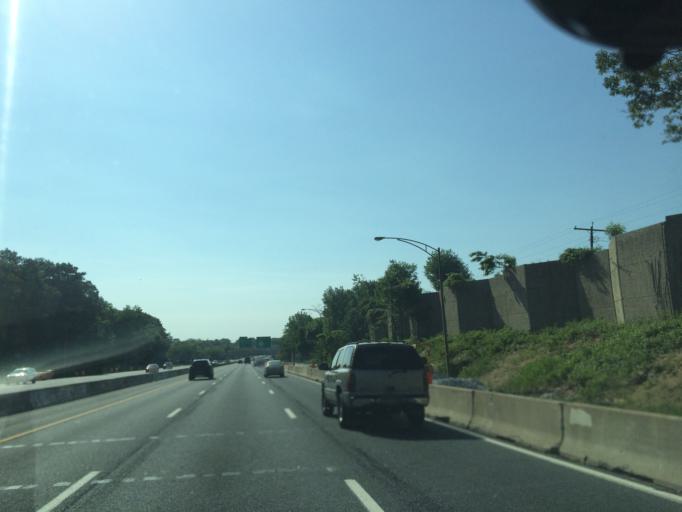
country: US
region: Maryland
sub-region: Baltimore County
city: Parkville
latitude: 39.3908
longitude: -76.5370
